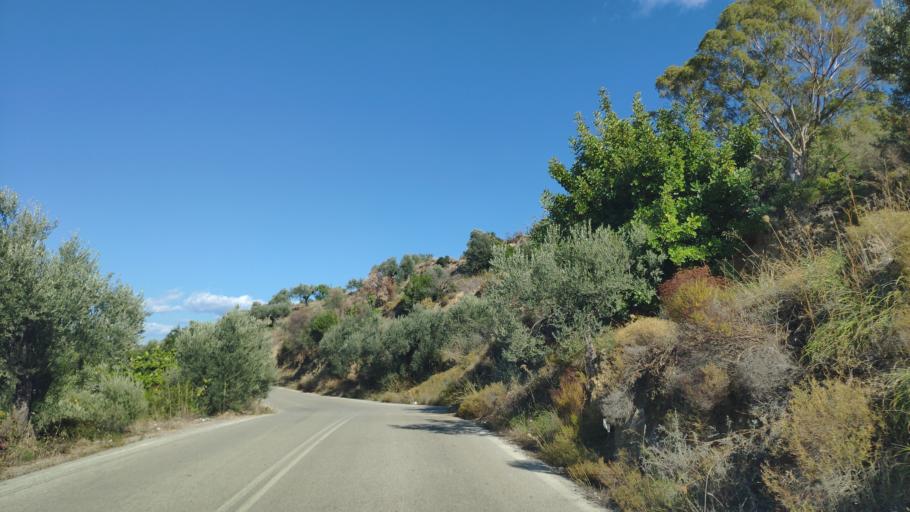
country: GR
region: Attica
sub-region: Nomos Piraios
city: Galatas
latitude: 37.5394
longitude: 23.3607
